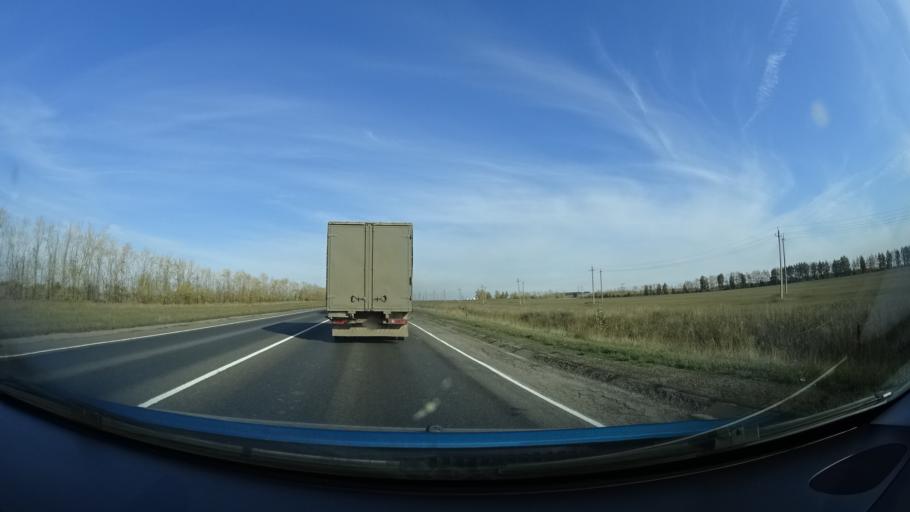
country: RU
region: Bashkortostan
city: Buzdyak
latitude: 54.6708
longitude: 54.7514
